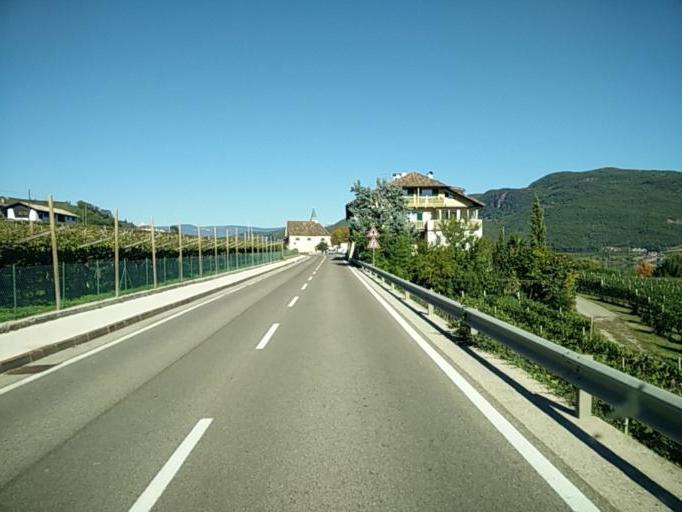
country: IT
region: Trentino-Alto Adige
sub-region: Bolzano
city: Termeno
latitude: 46.3745
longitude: 11.2515
